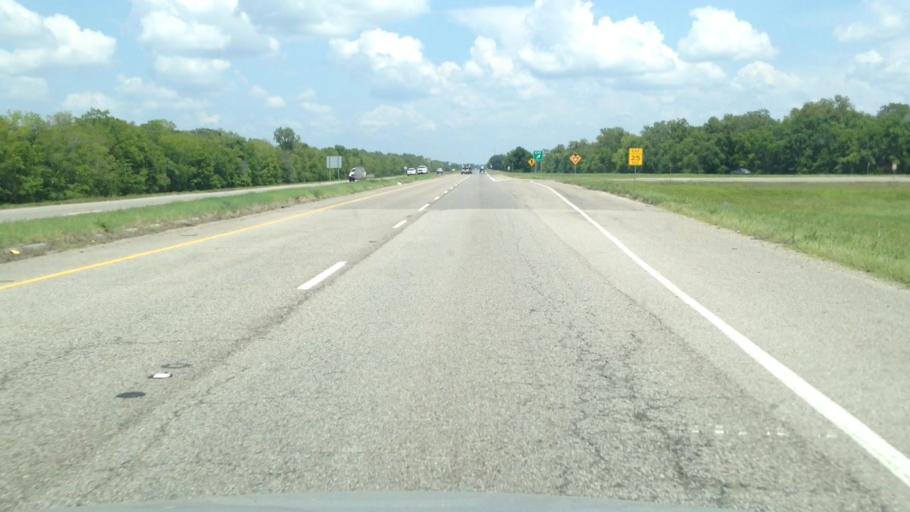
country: US
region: Louisiana
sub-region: Saint Landry Parish
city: Krotz Springs
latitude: 30.5454
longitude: -91.8116
